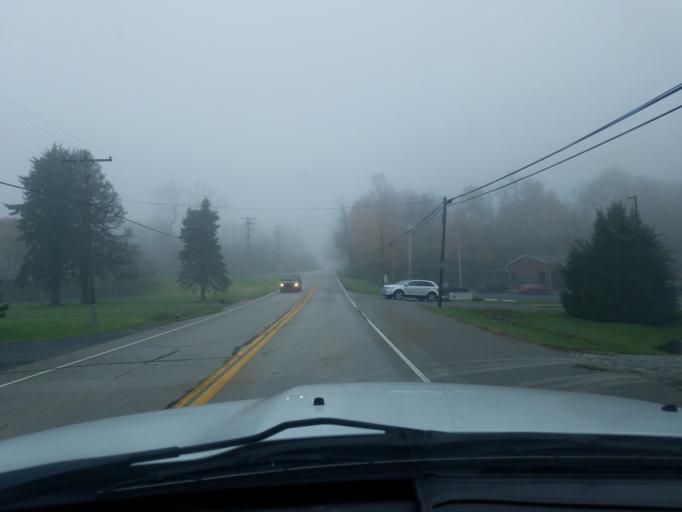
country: US
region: Indiana
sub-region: Floyd County
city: New Albany
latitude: 38.3254
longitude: -85.8768
